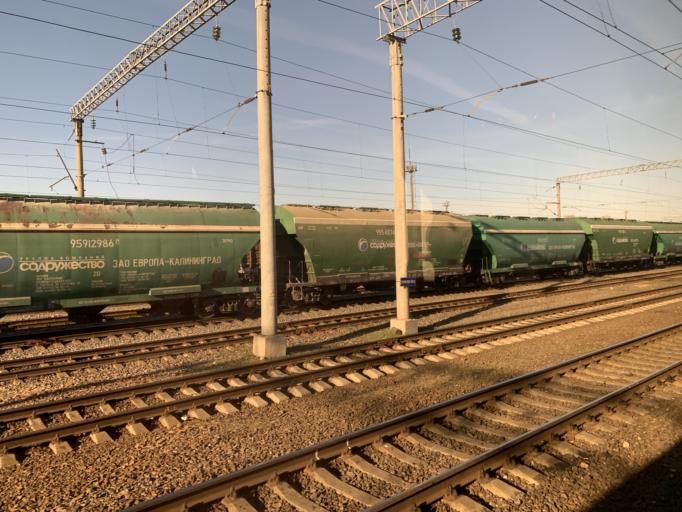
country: BY
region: Minsk
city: Maladzyechna
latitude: 54.3165
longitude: 26.8322
